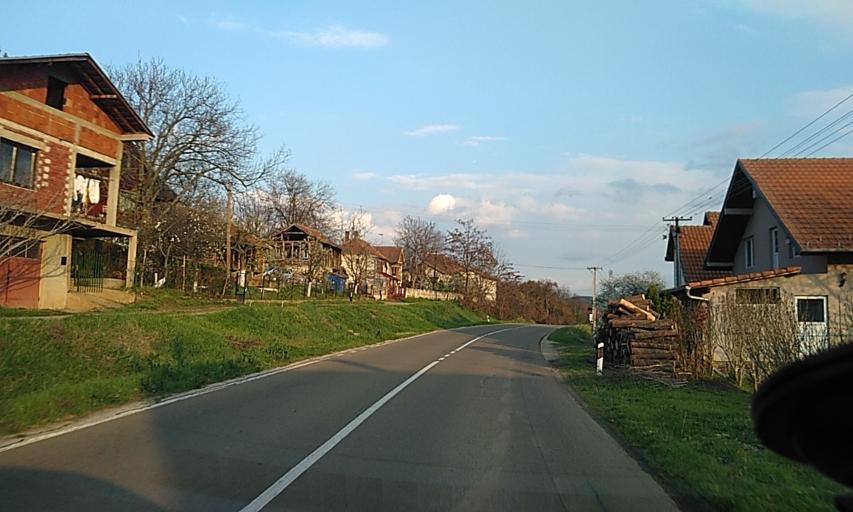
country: RS
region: Central Serbia
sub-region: Nisavski Okrug
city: Aleksinac
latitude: 43.5753
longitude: 21.6681
